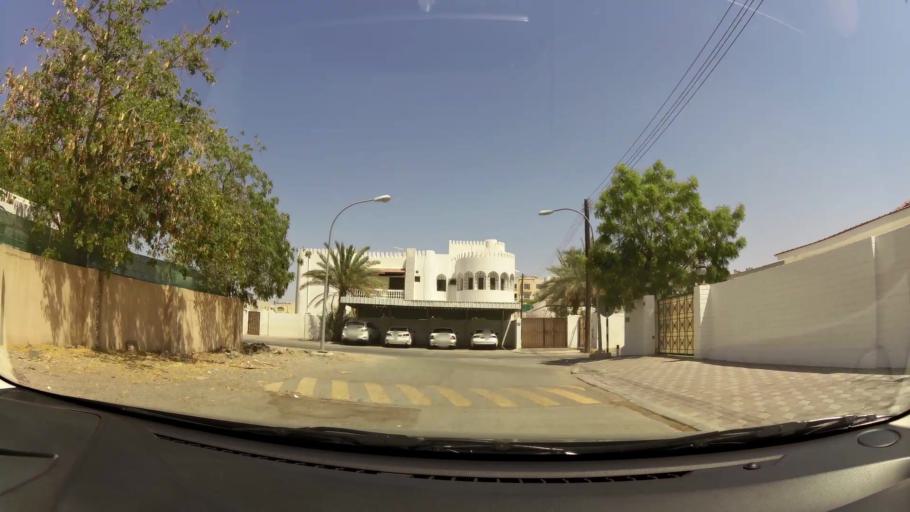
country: OM
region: Muhafazat Masqat
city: As Sib al Jadidah
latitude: 23.6298
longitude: 58.2310
